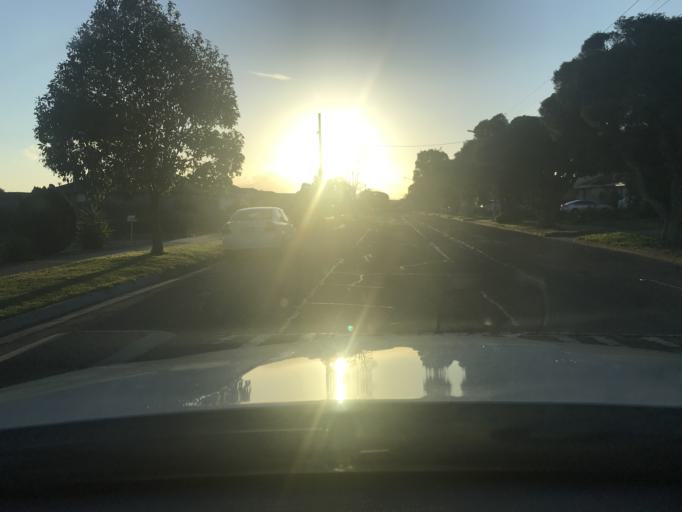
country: AU
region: Victoria
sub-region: Hume
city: Craigieburn
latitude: -37.5956
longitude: 144.9291
